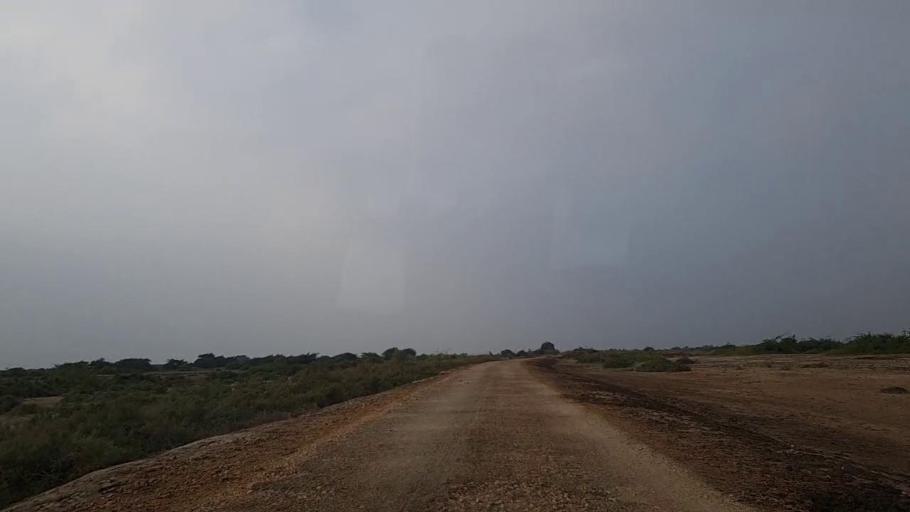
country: PK
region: Sindh
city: Mirpur Sakro
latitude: 24.6056
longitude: 67.5165
